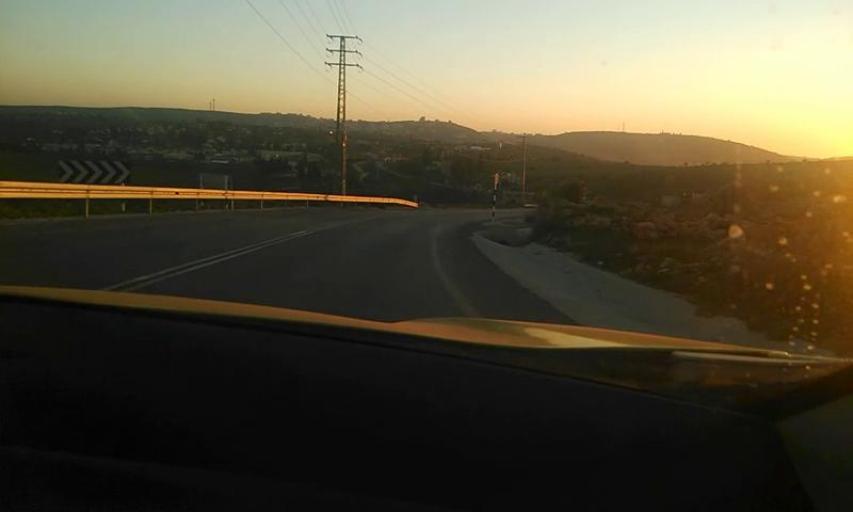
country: PS
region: West Bank
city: Silwad
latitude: 31.9648
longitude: 35.2653
